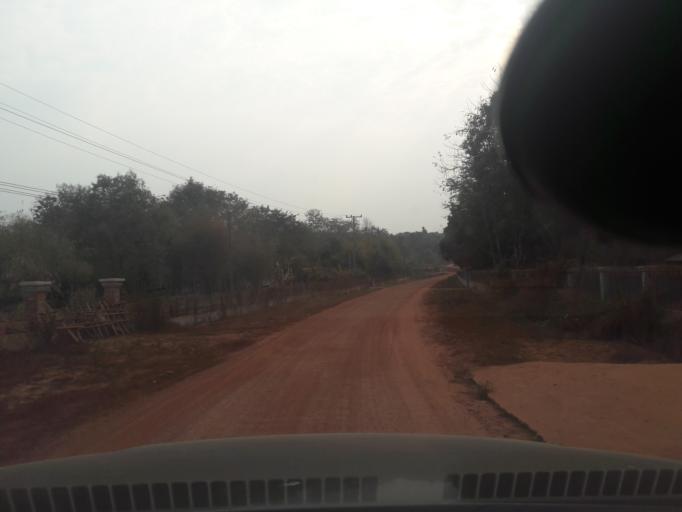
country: TH
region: Nong Khai
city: Si Chiang Mai
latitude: 18.0546
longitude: 102.4932
